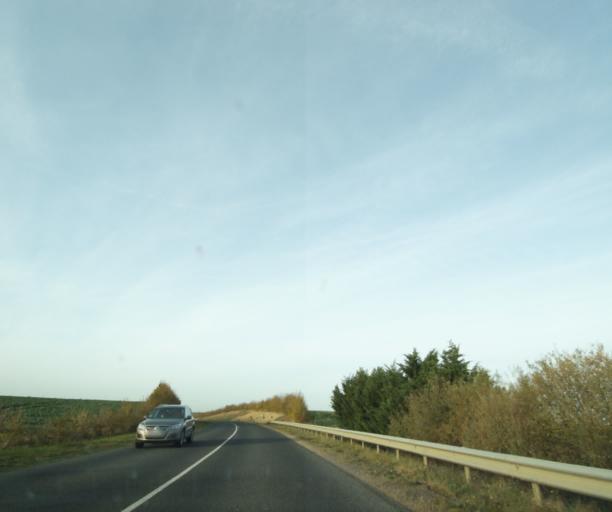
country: FR
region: Lorraine
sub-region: Departement de la Meuse
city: Etain
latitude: 49.1898
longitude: 5.6646
